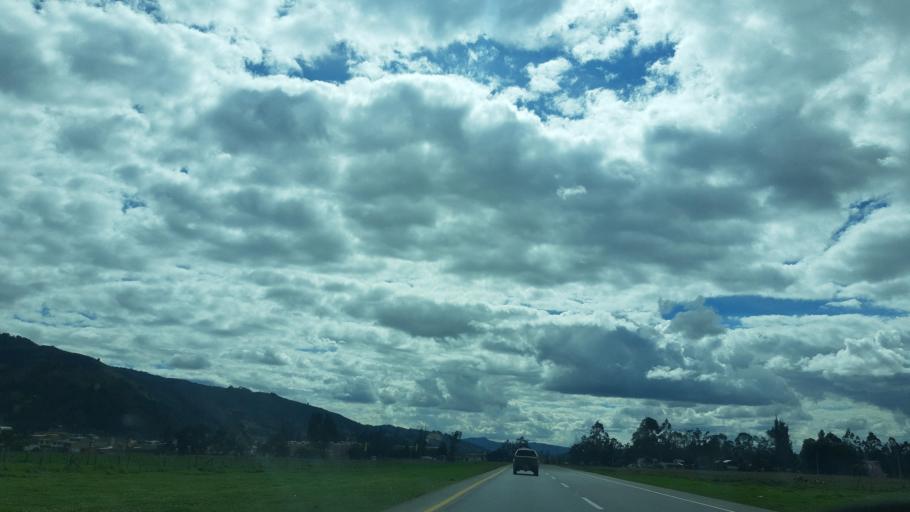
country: CO
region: Cundinamarca
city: Gachancipa
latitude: 4.9969
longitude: -73.8730
